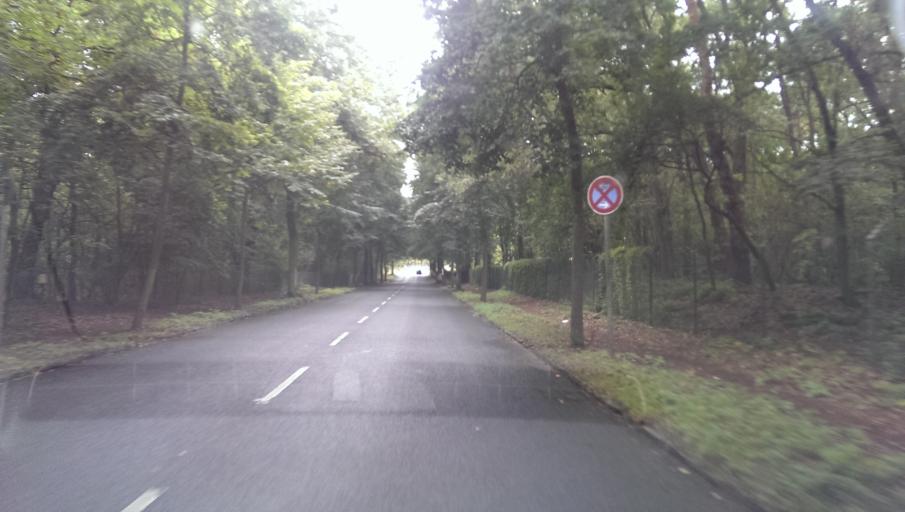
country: DE
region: Berlin
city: Haselhorst
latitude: 52.5193
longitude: 13.2183
